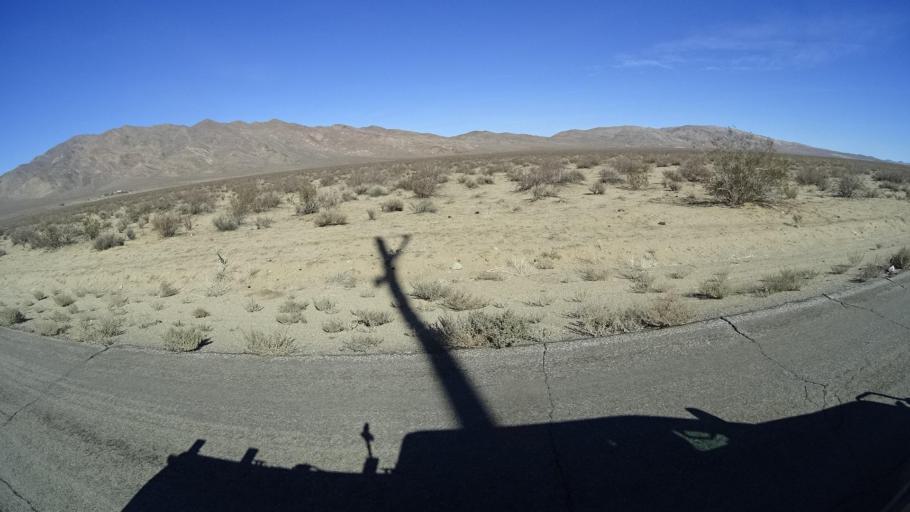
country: US
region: California
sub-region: Kern County
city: China Lake Acres
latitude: 35.3902
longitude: -117.7764
